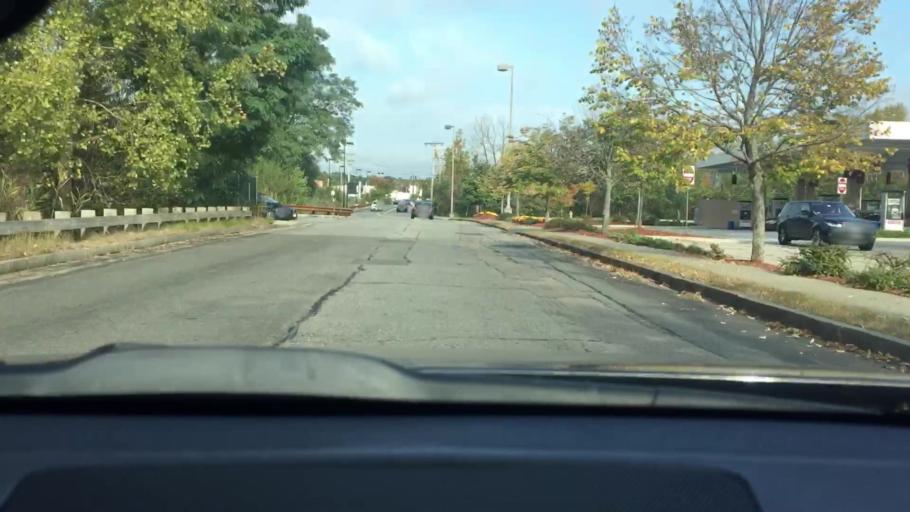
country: US
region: Massachusetts
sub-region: Norfolk County
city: Dedham
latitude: 42.2307
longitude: -71.1746
